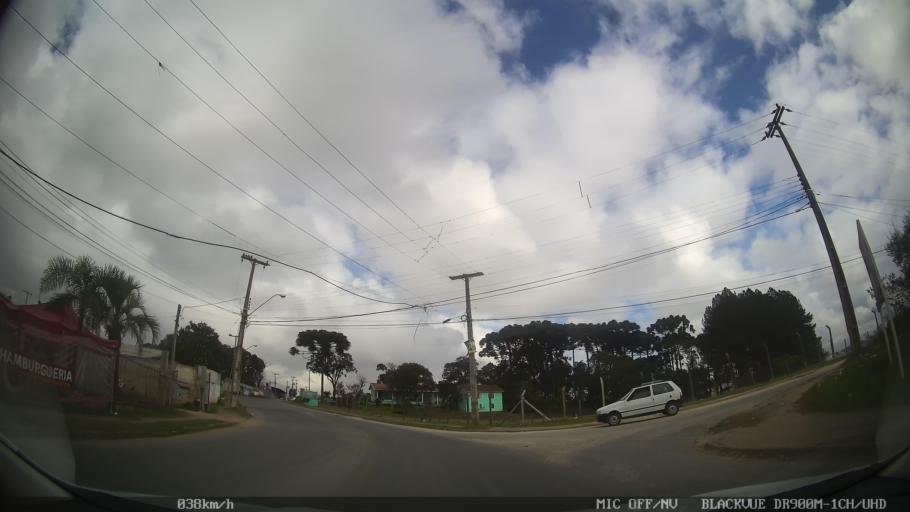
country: BR
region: Parana
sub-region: Colombo
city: Colombo
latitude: -25.3433
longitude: -49.2423
